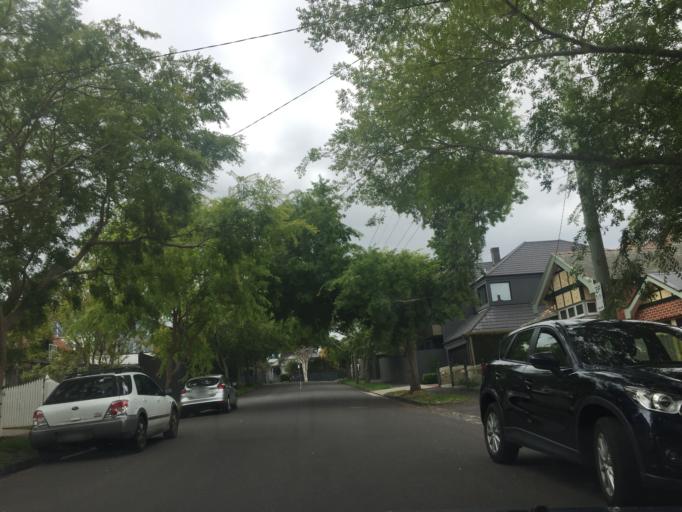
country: AU
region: Victoria
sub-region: Boroondara
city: Kew
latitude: -37.8112
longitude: 145.0413
